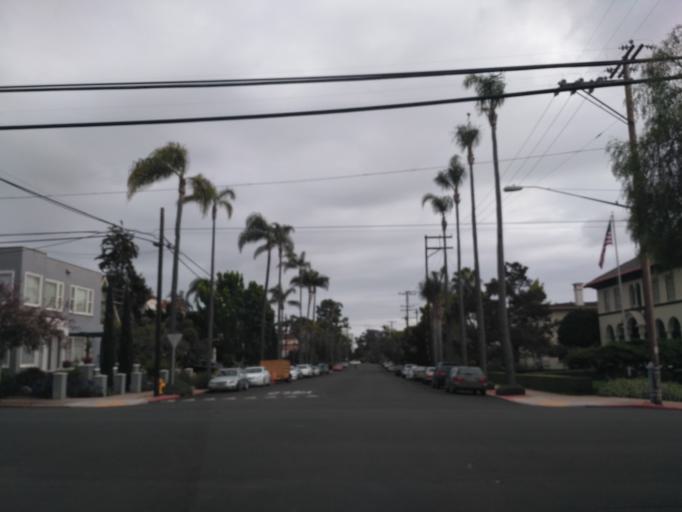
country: US
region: California
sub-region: San Diego County
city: San Diego
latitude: 32.7389
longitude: -117.1631
